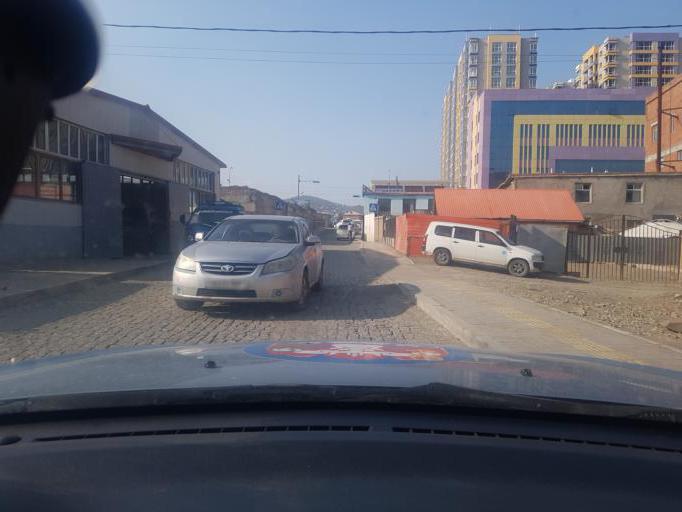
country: MN
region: Ulaanbaatar
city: Ulaanbaatar
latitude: 47.9231
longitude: 106.9666
